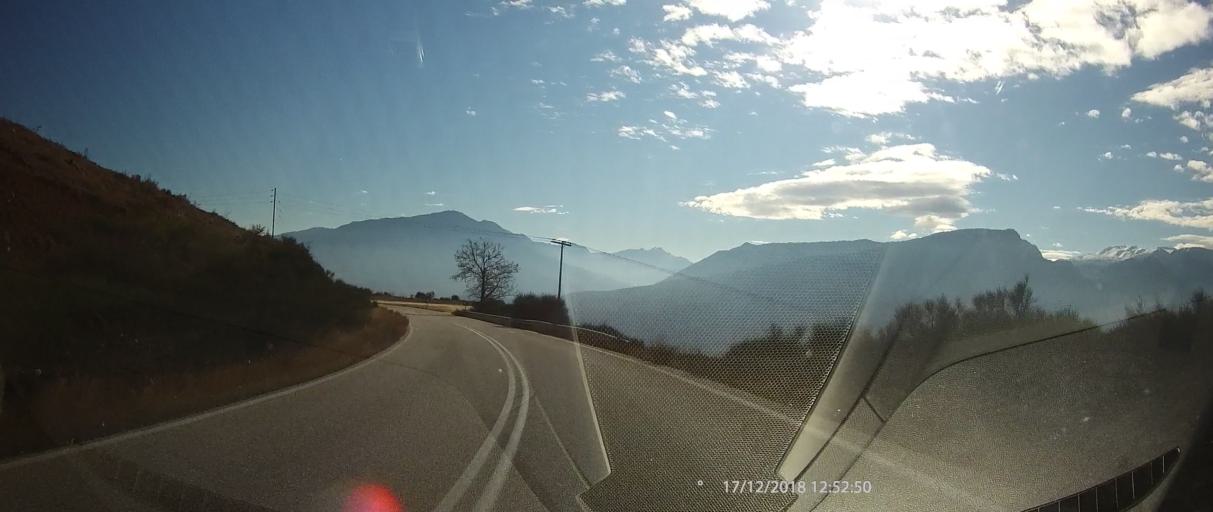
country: GR
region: Thessaly
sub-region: Trikala
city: Kastraki
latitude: 39.7570
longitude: 21.4831
